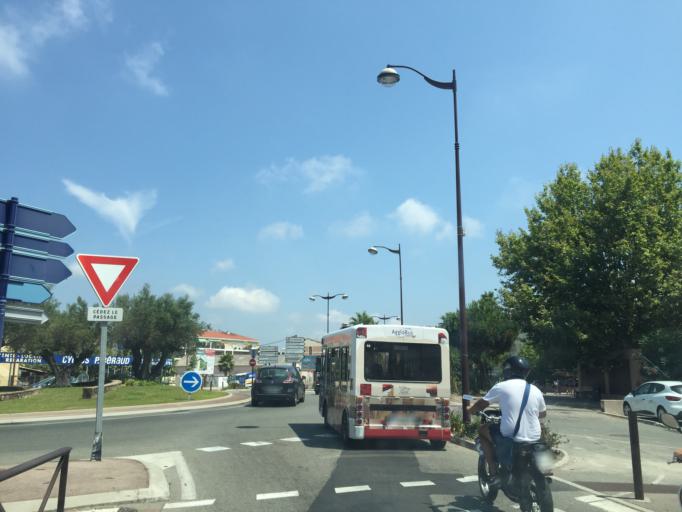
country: FR
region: Provence-Alpes-Cote d'Azur
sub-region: Departement du Var
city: Frejus
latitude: 43.4272
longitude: 6.7486
